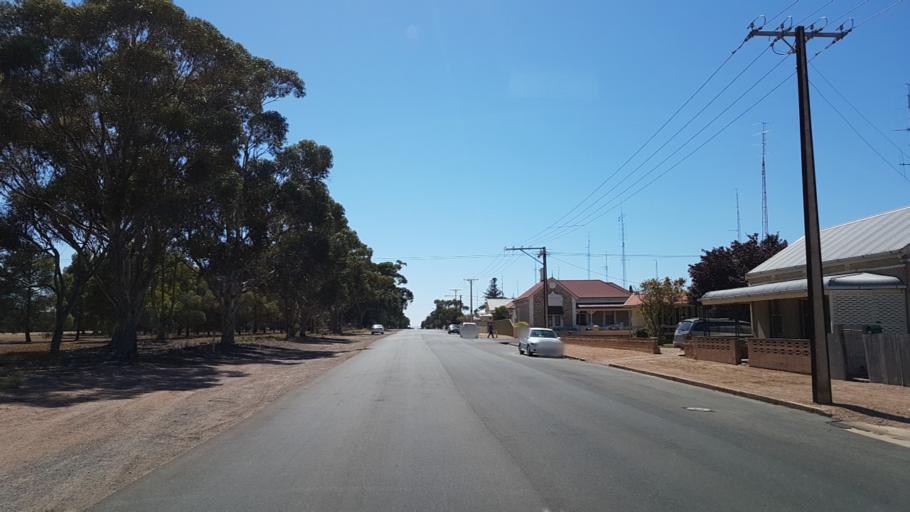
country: AU
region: South Australia
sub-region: Copper Coast
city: Kadina
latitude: -33.9583
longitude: 137.7135
